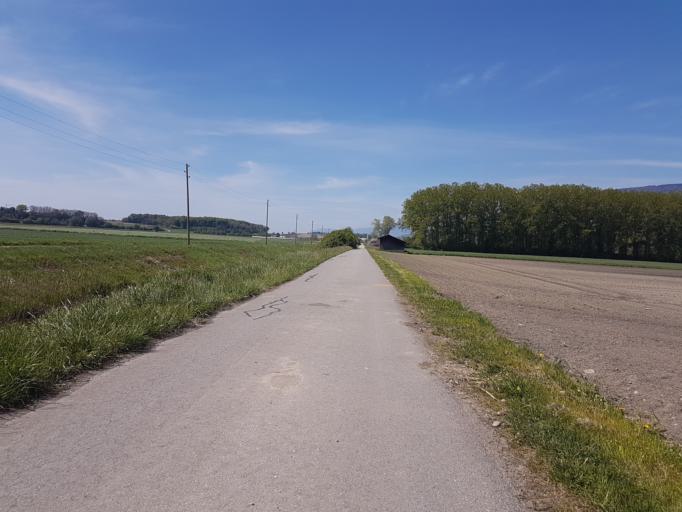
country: CH
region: Neuchatel
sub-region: Neuchatel District
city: Le Landeron
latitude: 47.0403
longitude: 7.0581
